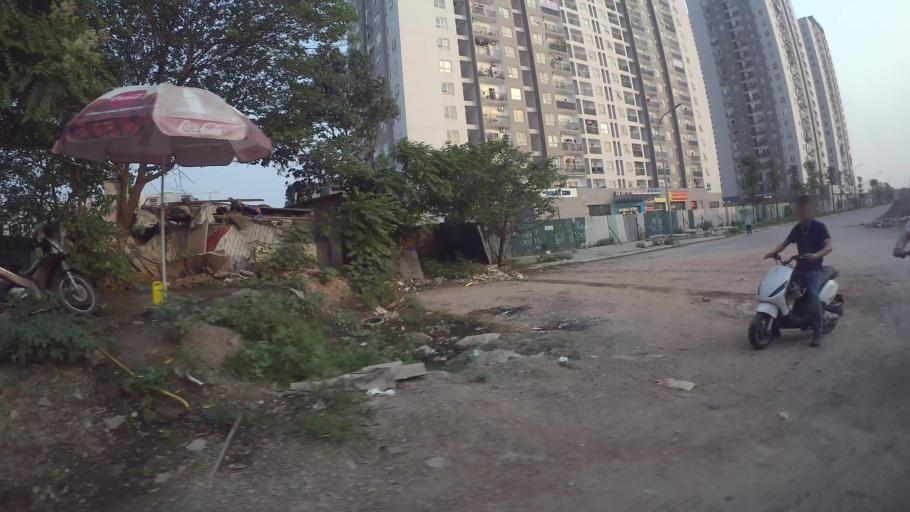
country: VN
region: Ha Noi
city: Thanh Xuan
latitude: 20.9763
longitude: 105.8206
